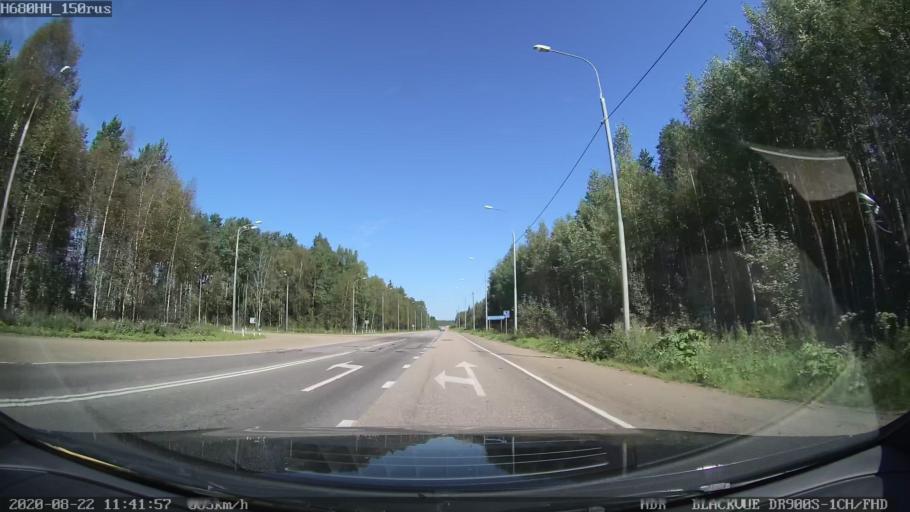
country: RU
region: Tverskaya
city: Sakharovo
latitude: 56.9952
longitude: 36.0260
